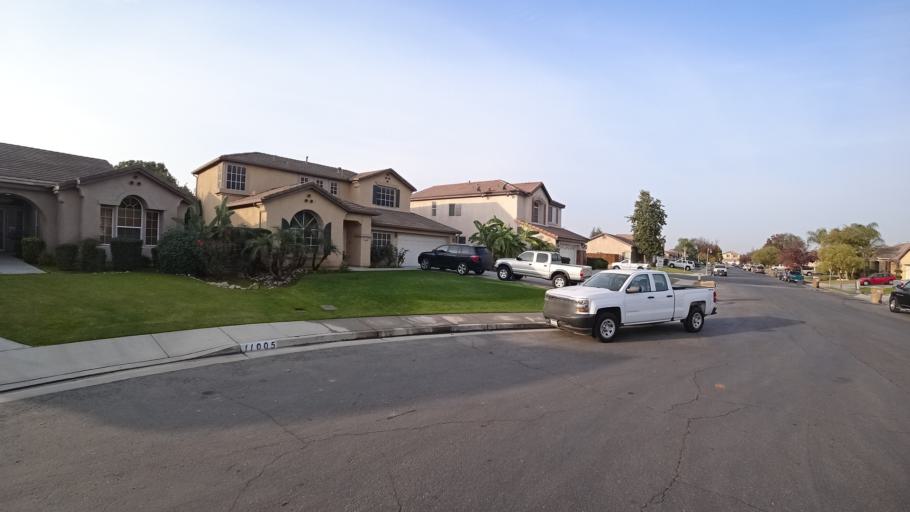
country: US
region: California
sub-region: Kern County
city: Greenacres
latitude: 35.4237
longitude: -119.1244
